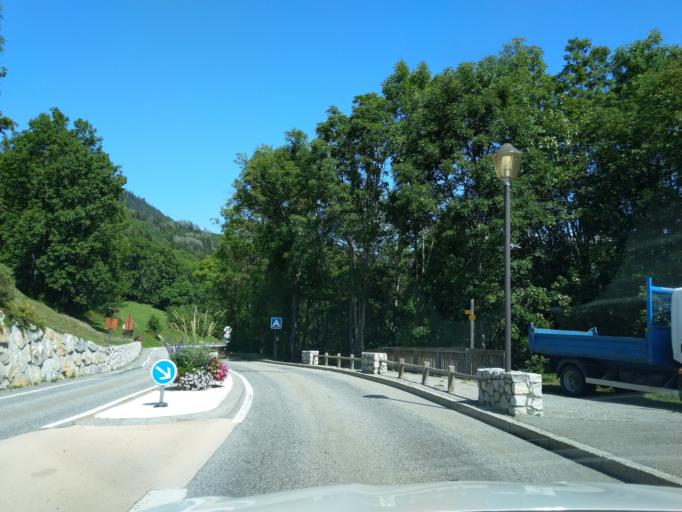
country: FR
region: Rhone-Alpes
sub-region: Departement de la Savoie
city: Les Allues
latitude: 45.4353
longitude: 6.5559
